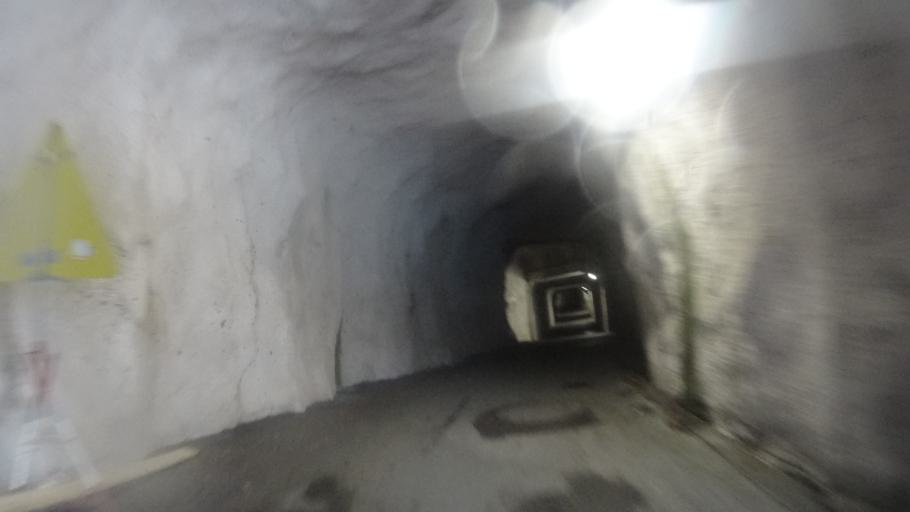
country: CH
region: Saint Gallen
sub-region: Wahlkreis See-Gaster
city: Amden
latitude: 47.1249
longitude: 9.1401
